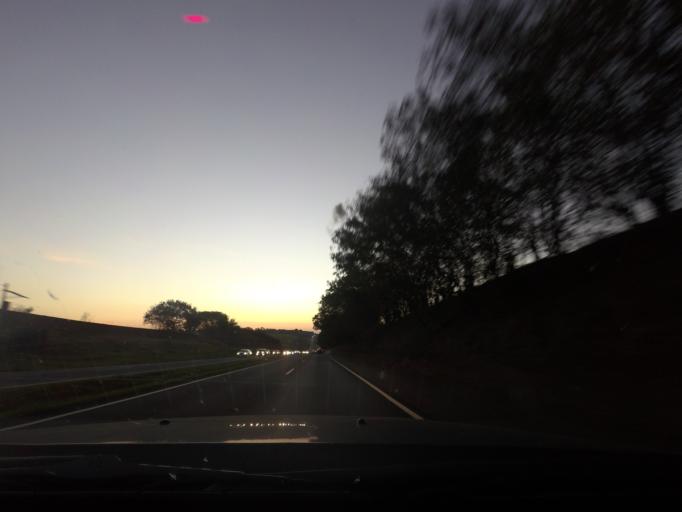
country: BR
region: Sao Paulo
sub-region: Piracicaba
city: Piracicaba
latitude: -22.7250
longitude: -47.5734
